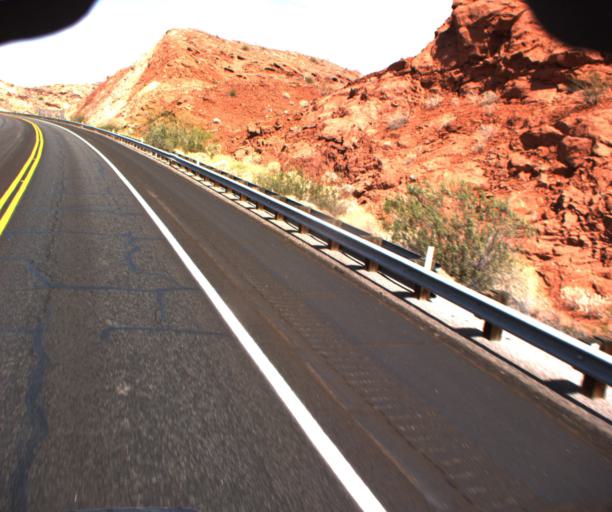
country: US
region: Arizona
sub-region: La Paz County
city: Cienega Springs
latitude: 34.2449
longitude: -114.1657
